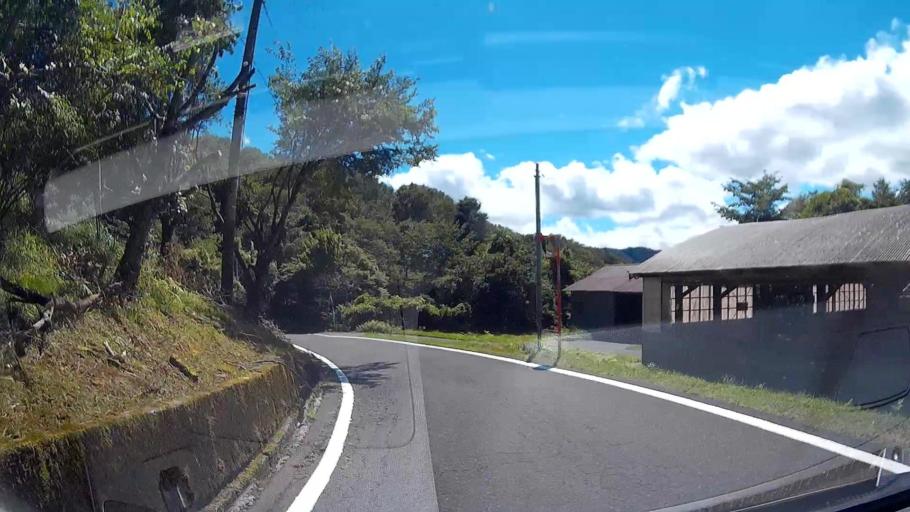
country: JP
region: Shizuoka
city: Shizuoka-shi
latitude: 35.2030
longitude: 138.2583
